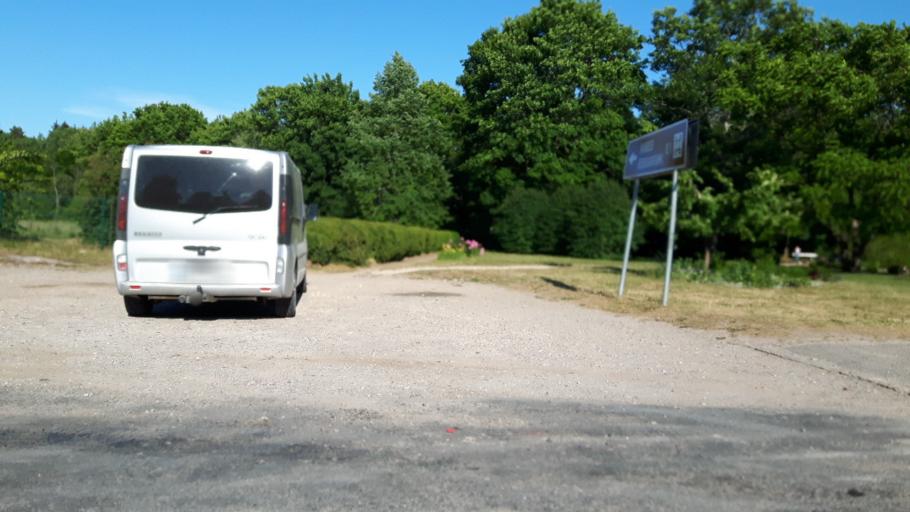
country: LV
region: Talsu Rajons
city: Stende
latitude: 57.0683
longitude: 22.2936
